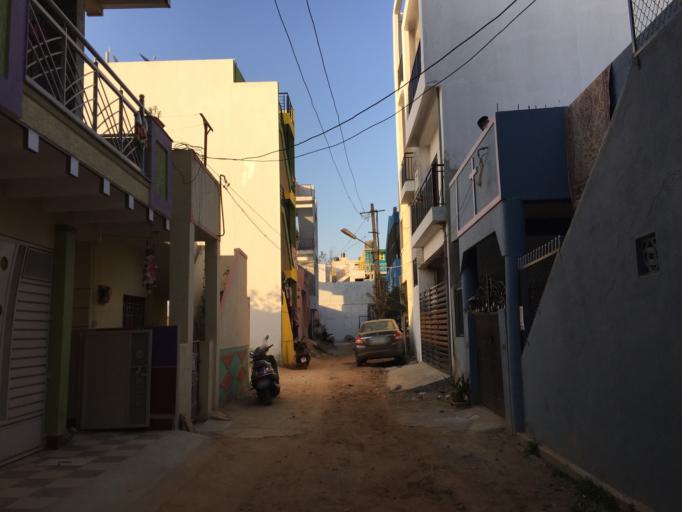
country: IN
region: Karnataka
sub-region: Bangalore Urban
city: Yelahanka
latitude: 13.0535
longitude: 77.6300
